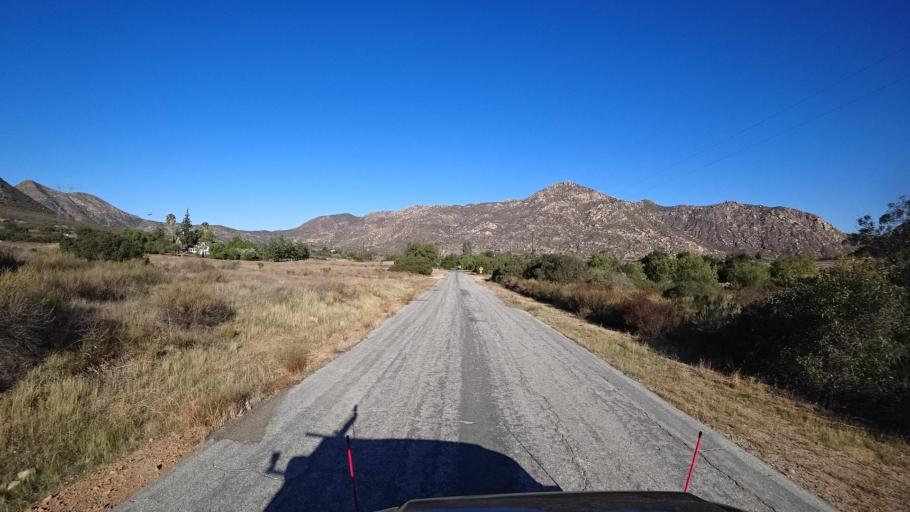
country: MX
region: Baja California
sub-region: Tecate
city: Lomas de Santa Anita
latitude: 32.6062
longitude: -116.6941
